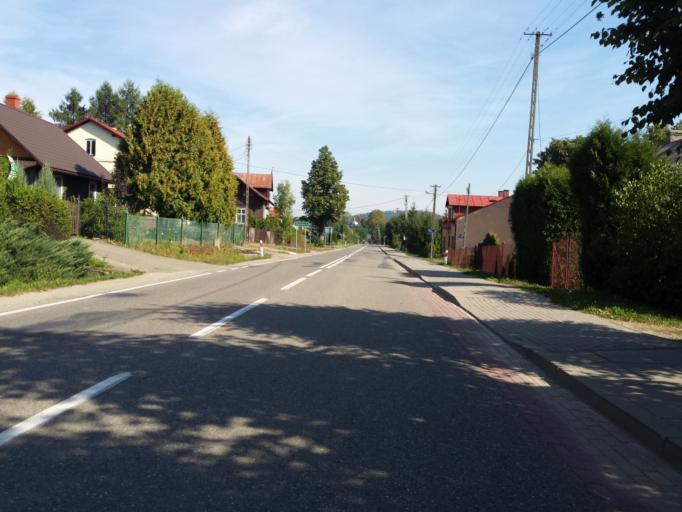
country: PL
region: Subcarpathian Voivodeship
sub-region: Powiat leski
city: Baligrod
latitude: 49.3303
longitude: 22.2854
